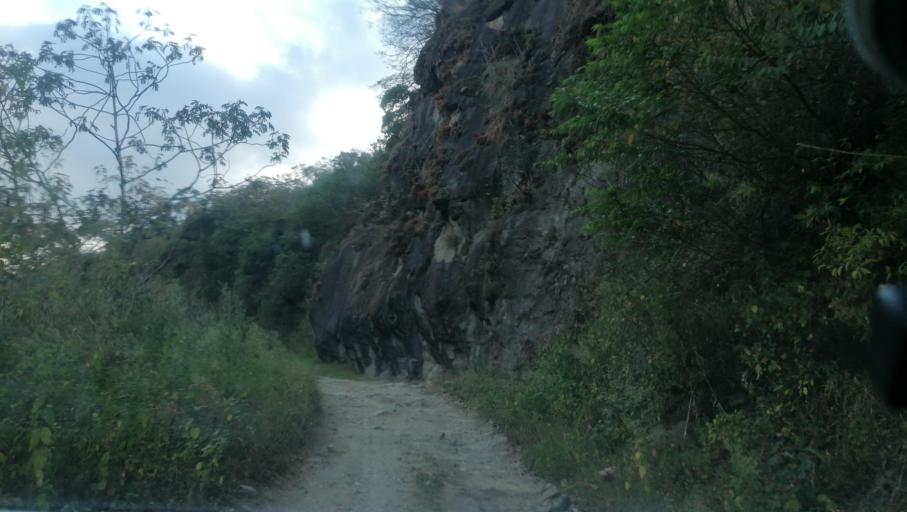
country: MX
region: Chiapas
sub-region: Cacahoatan
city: Benito Juarez
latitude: 15.1449
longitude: -92.1880
